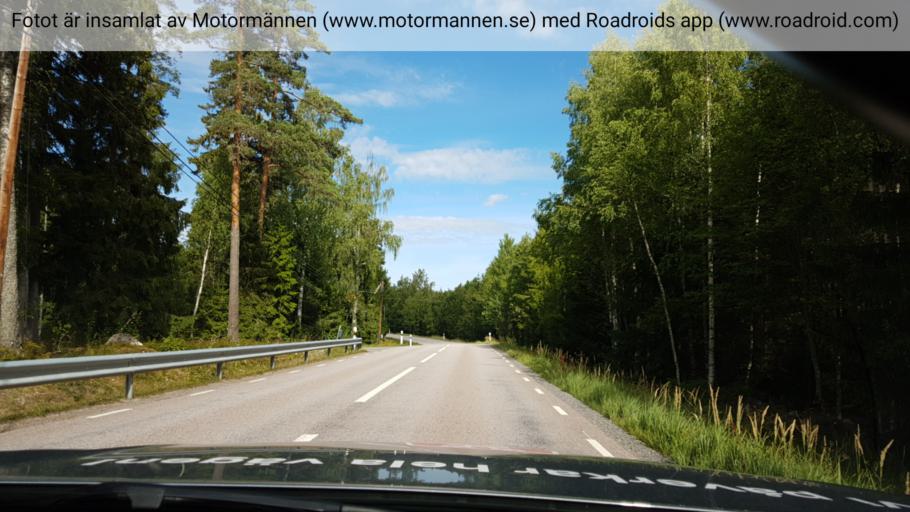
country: SE
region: Uppsala
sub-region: Heby Kommun
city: OEstervala
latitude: 60.0150
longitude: 17.2882
